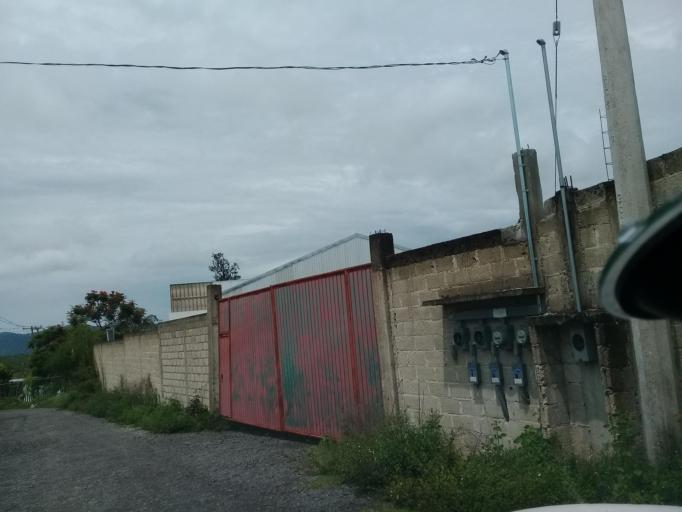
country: MX
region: Veracruz
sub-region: Emiliano Zapata
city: Dos Rios
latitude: 19.4696
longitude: -96.7768
